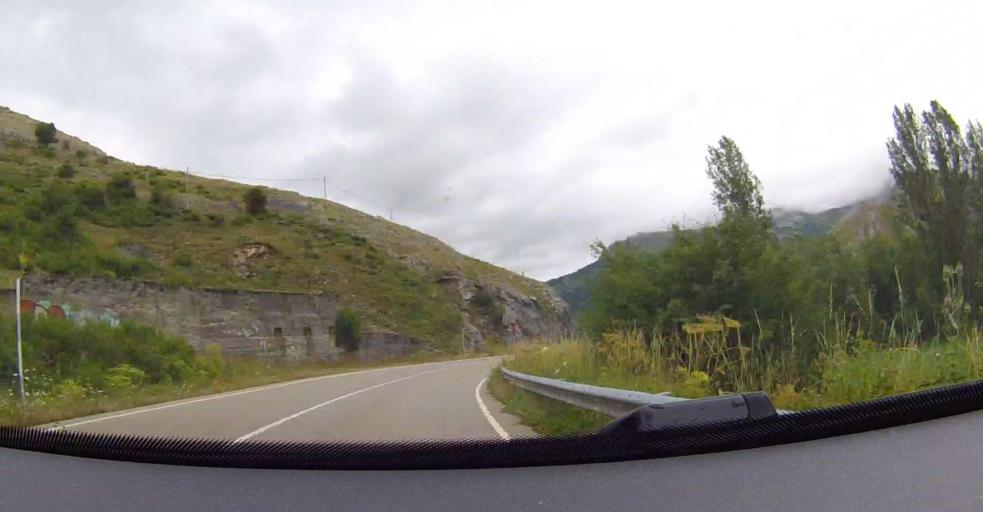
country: ES
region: Castille and Leon
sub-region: Provincia de Leon
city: Buron
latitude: 43.0280
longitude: -5.0649
